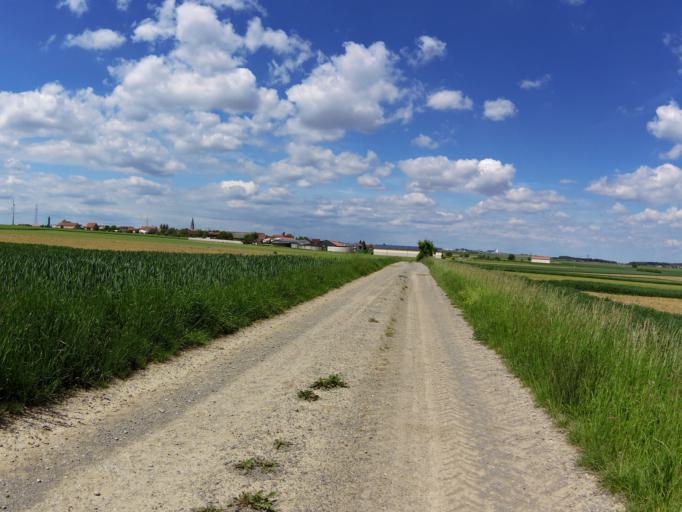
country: DE
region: Bavaria
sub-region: Regierungsbezirk Unterfranken
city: Biebelried
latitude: 49.7383
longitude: 10.0713
